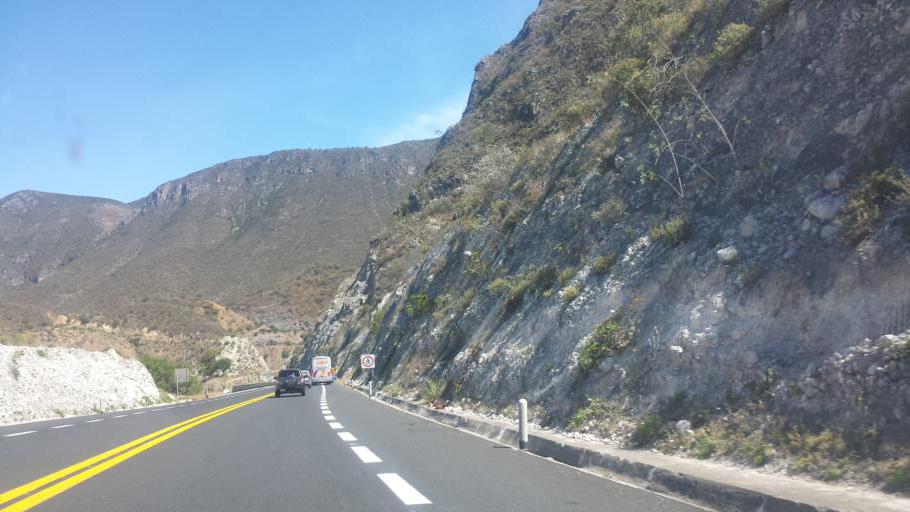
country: MX
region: Puebla
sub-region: San Jose Miahuatlan
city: San Pedro Tetitlan
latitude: 18.0881
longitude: -97.3488
